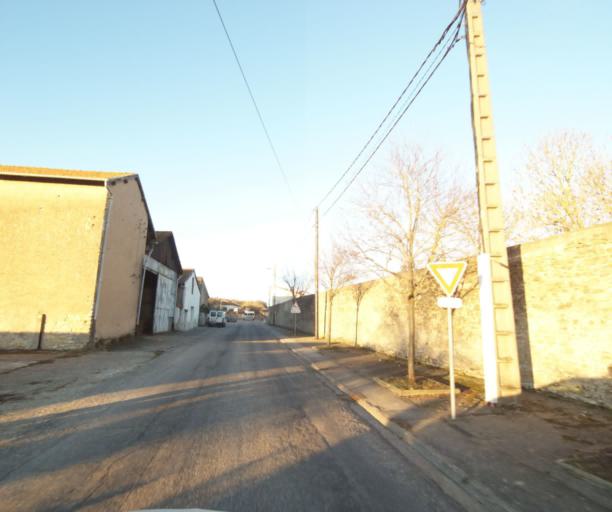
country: FR
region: Lorraine
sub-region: Departement de Meurthe-et-Moselle
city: Laneuveville-devant-Nancy
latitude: 48.6628
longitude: 6.2414
